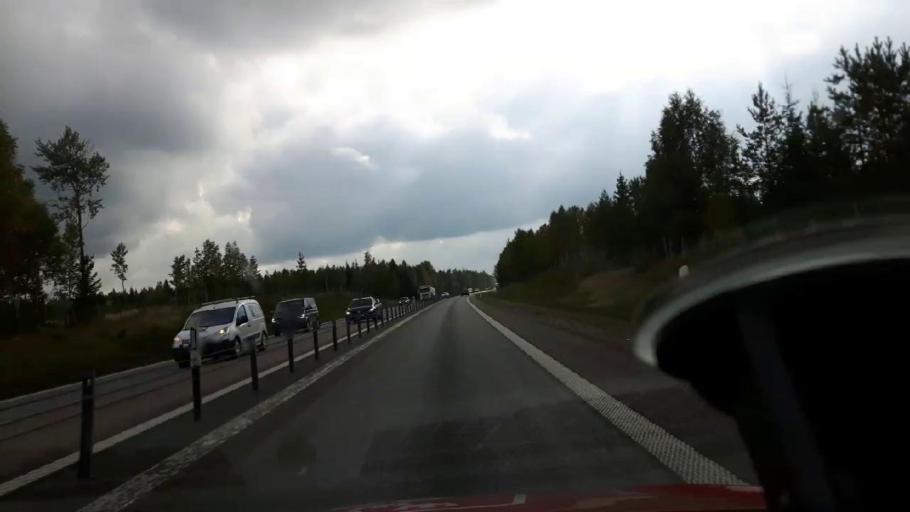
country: SE
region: Gaevleborg
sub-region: Gavle Kommun
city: Norrsundet
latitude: 60.8203
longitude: 17.0845
